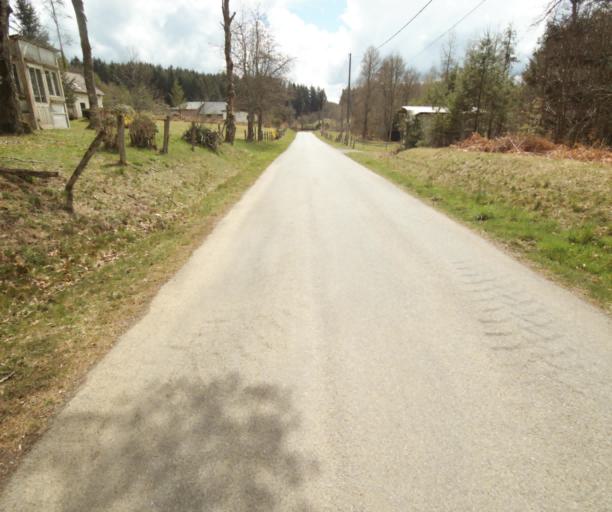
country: FR
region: Limousin
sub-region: Departement de la Correze
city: Correze
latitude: 45.3272
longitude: 1.9168
